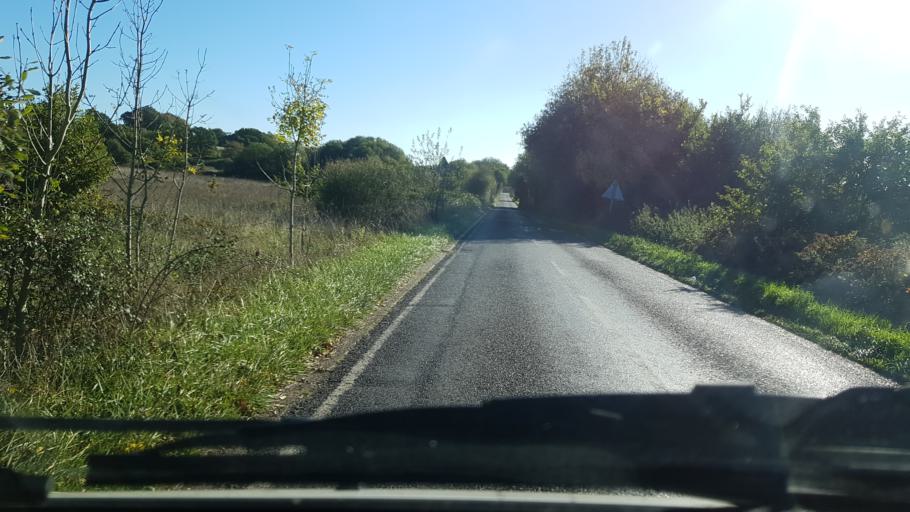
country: GB
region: England
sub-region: Surrey
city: Cranleigh
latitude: 51.1626
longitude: -0.5012
